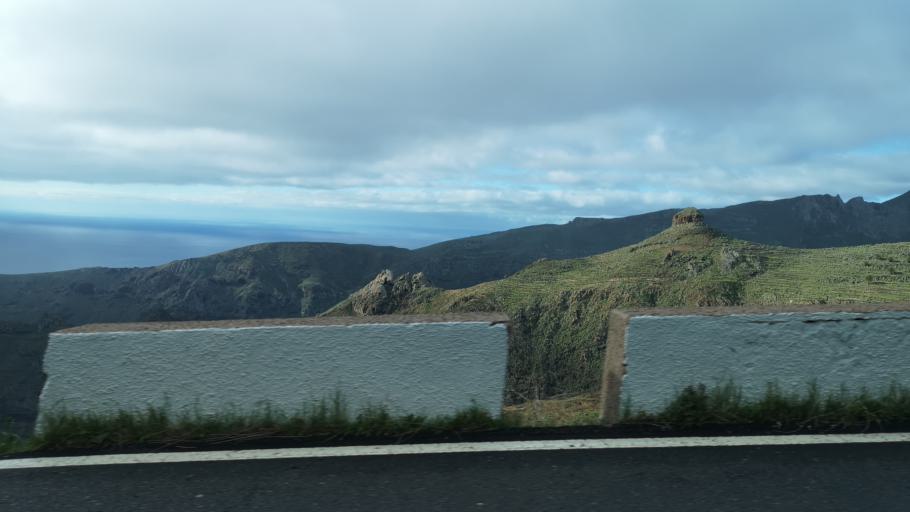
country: ES
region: Canary Islands
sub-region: Provincia de Santa Cruz de Tenerife
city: San Sebastian de la Gomera
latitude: 28.0948
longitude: -17.1551
